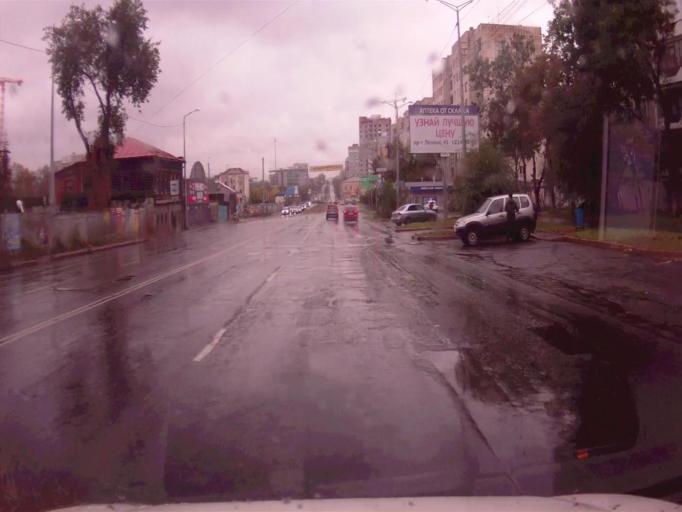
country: RU
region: Chelyabinsk
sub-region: Gorod Chelyabinsk
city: Chelyabinsk
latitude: 55.1647
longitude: 61.4161
